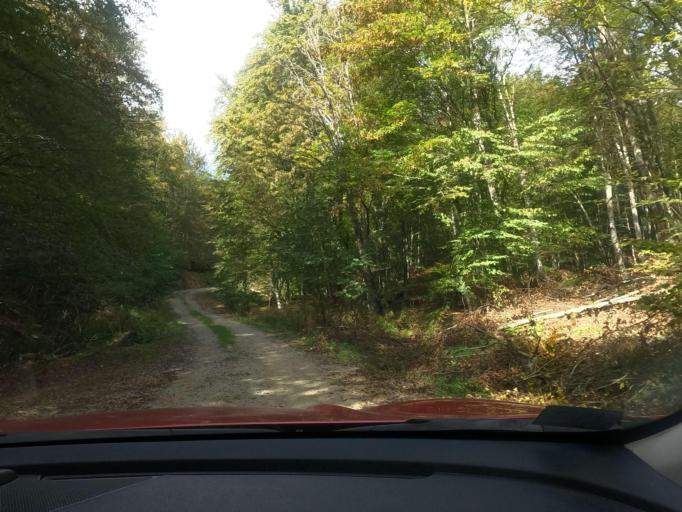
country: BA
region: Federation of Bosnia and Herzegovina
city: Velika Kladusa
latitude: 45.2442
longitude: 15.7731
